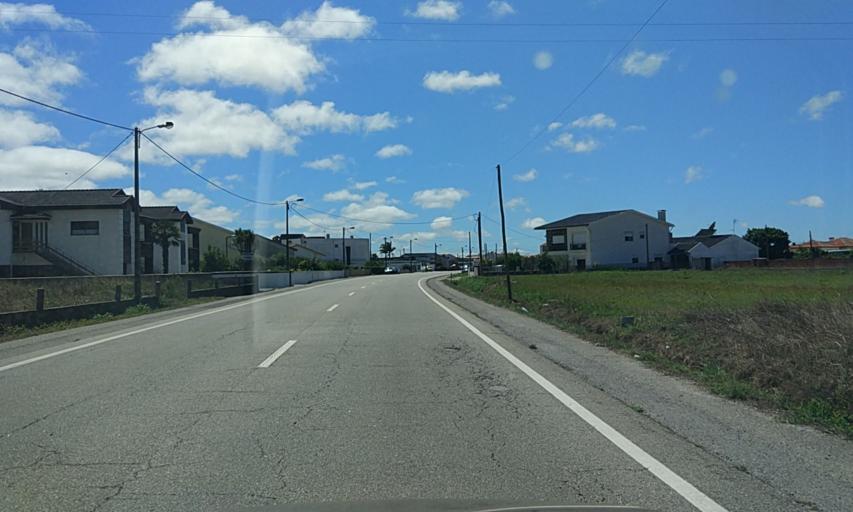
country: PT
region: Aveiro
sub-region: Vagos
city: Vagos
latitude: 40.4878
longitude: -8.6875
